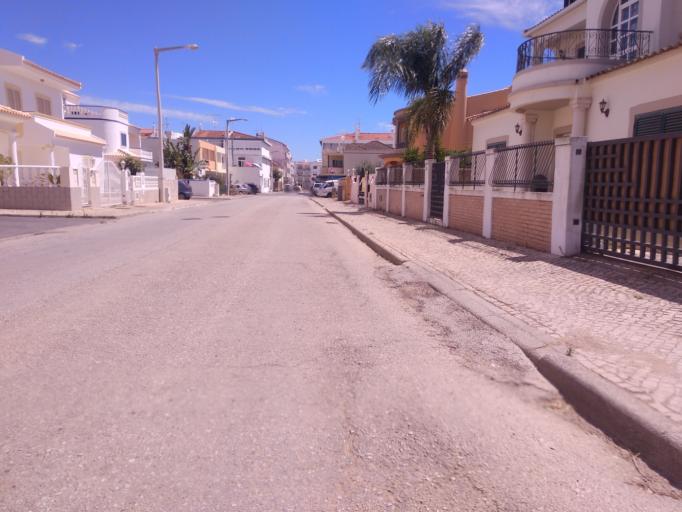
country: PT
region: Faro
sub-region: Sao Bras de Alportel
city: Sao Bras de Alportel
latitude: 37.1539
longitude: -7.8830
